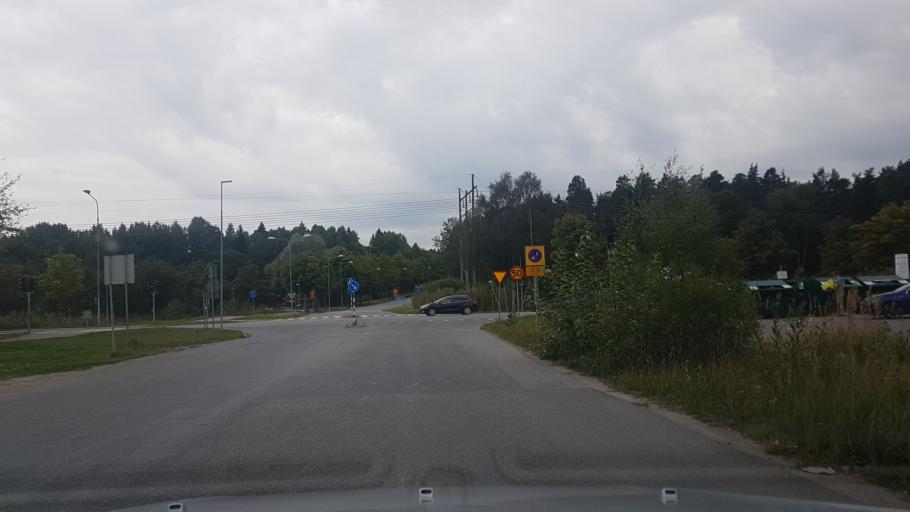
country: SE
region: Stockholm
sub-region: Jarfalla Kommun
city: Jakobsberg
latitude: 59.4168
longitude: 17.8241
